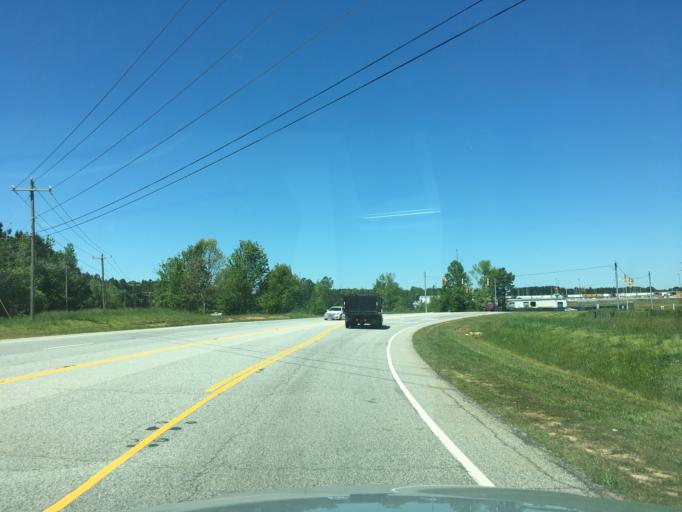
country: US
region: South Carolina
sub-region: Greenville County
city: Greer
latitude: 34.8901
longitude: -82.1963
